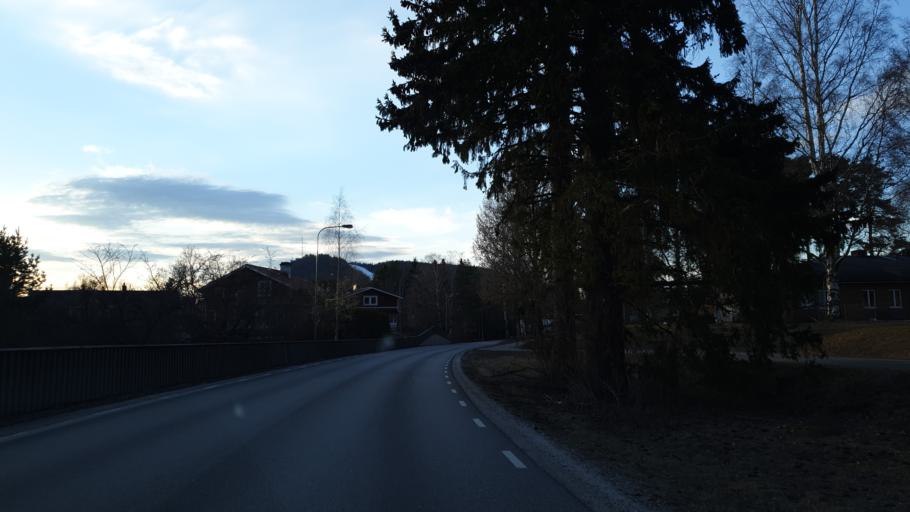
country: SE
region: Vaesternorrland
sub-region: Sundsvalls Kommun
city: Skottsund
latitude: 62.2898
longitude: 17.3885
